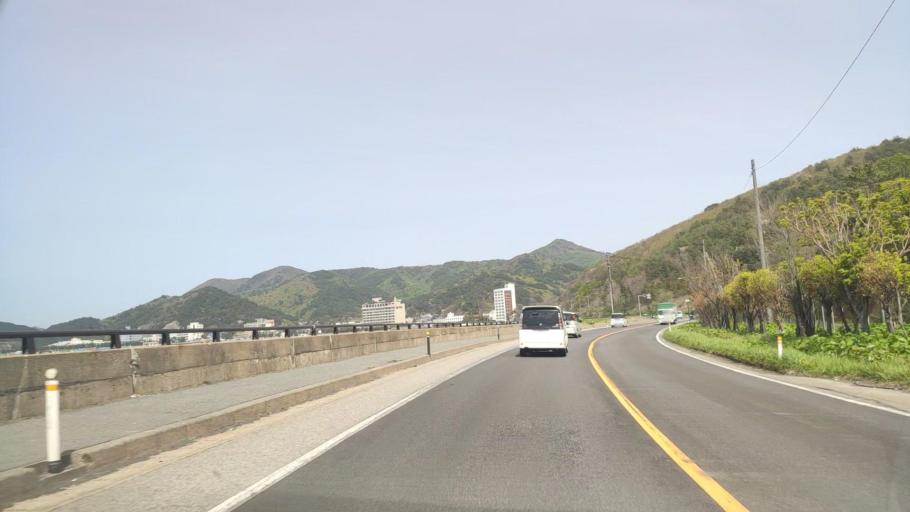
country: JP
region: Aomori
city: Aomori Shi
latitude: 40.8850
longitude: 140.8527
